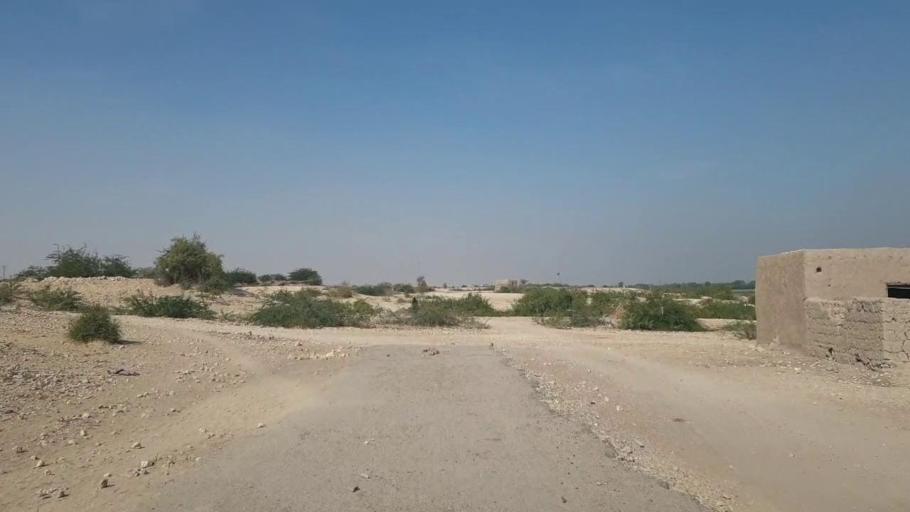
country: PK
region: Sindh
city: Hala
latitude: 25.7351
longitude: 68.2959
